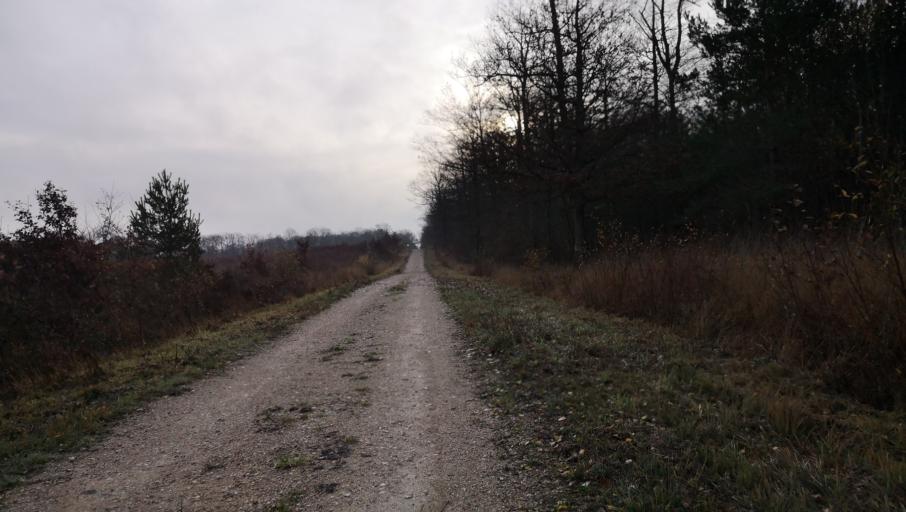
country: FR
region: Centre
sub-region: Departement du Loiret
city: Chanteau
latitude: 47.9482
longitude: 1.9637
